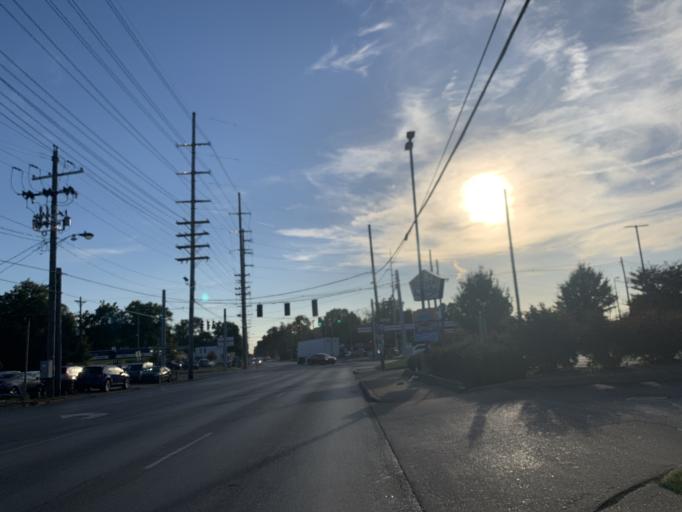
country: US
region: Kentucky
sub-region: Jefferson County
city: Louisville
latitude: 38.2206
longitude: -85.7769
